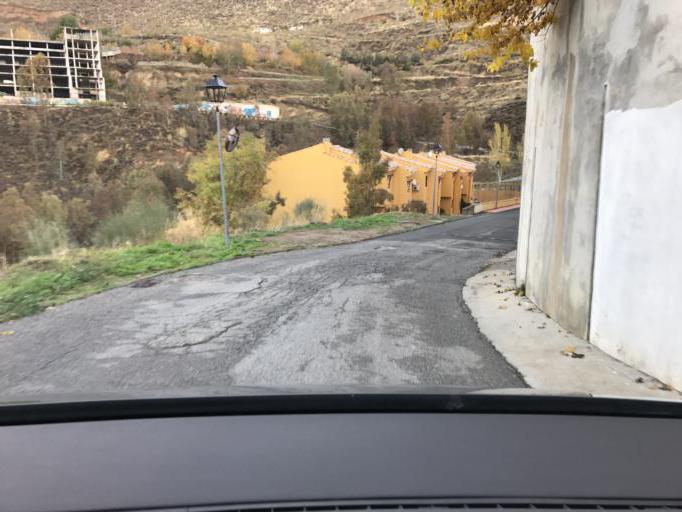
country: ES
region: Andalusia
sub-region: Provincia de Granada
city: Cenes de la Vega
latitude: 37.1640
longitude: -3.5429
